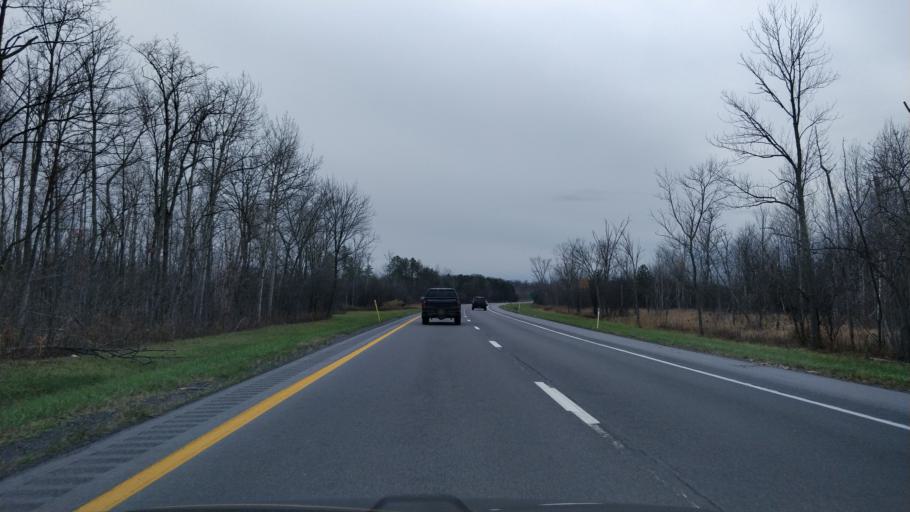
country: US
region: New York
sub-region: Jefferson County
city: Adams
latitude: 43.7547
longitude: -76.0598
